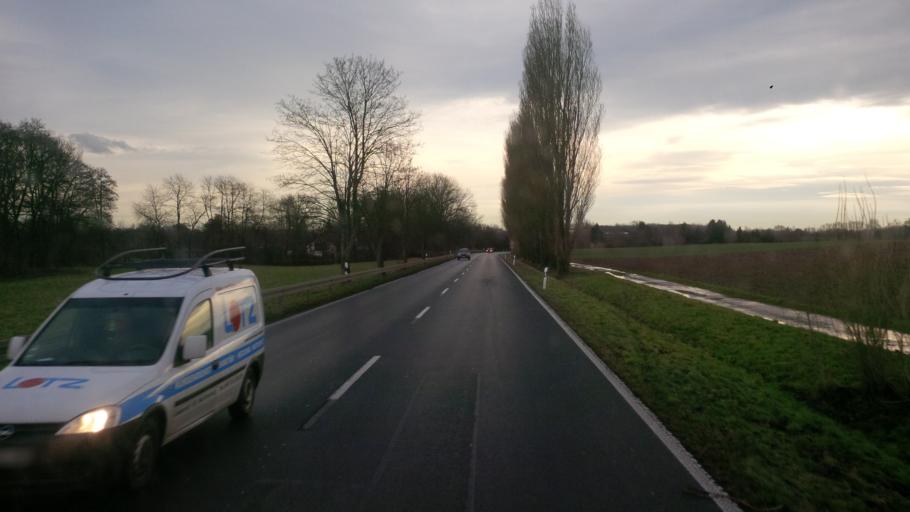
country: DE
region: Hesse
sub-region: Regierungsbezirk Darmstadt
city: Oberursel
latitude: 50.2189
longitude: 8.5949
